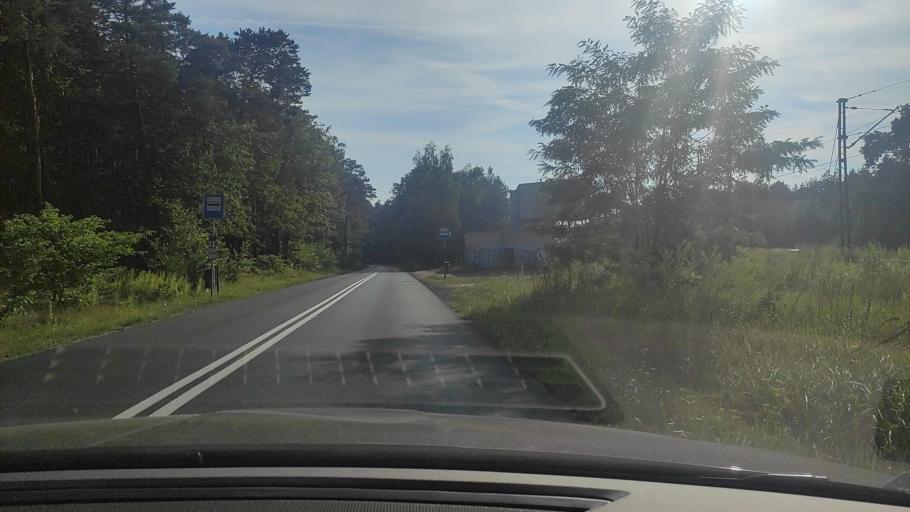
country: PL
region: Greater Poland Voivodeship
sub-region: Powiat poznanski
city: Swarzedz
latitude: 52.3954
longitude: 17.0384
